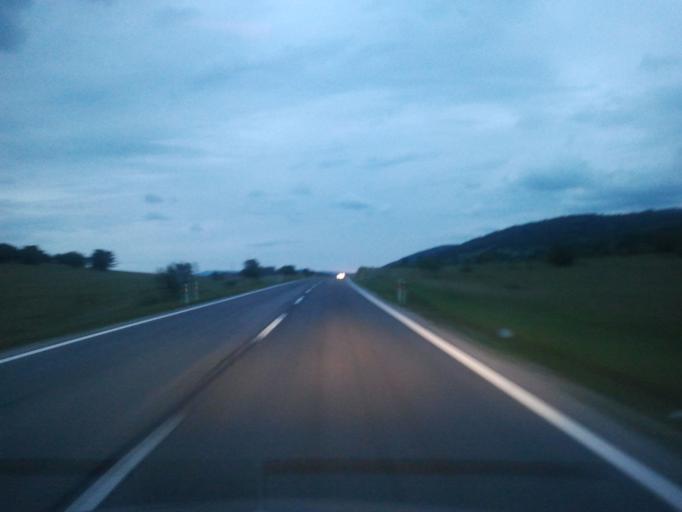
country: HR
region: Zadarska
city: Gracac
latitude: 44.4663
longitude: 15.8008
